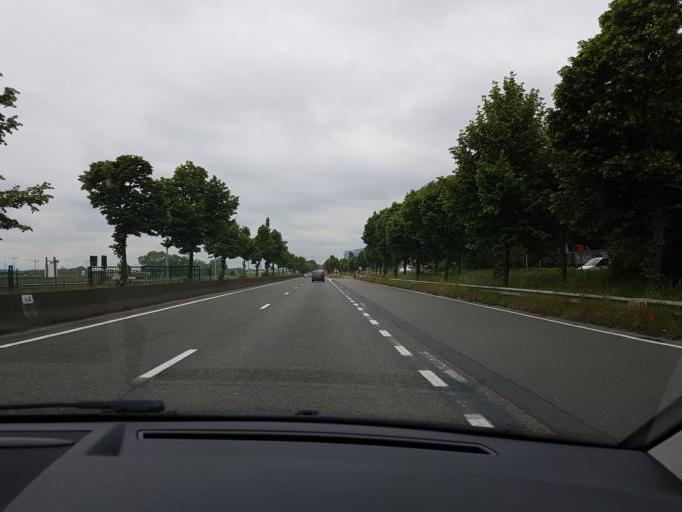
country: BE
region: Flanders
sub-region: Provincie Oost-Vlaanderen
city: Merelbeke
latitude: 51.0094
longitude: 3.7476
